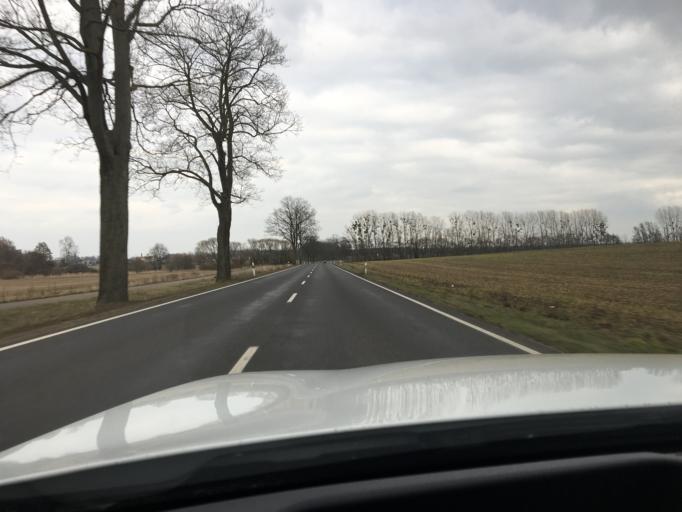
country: DE
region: Brandenburg
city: Liebenwalde
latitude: 52.8744
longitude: 13.4199
